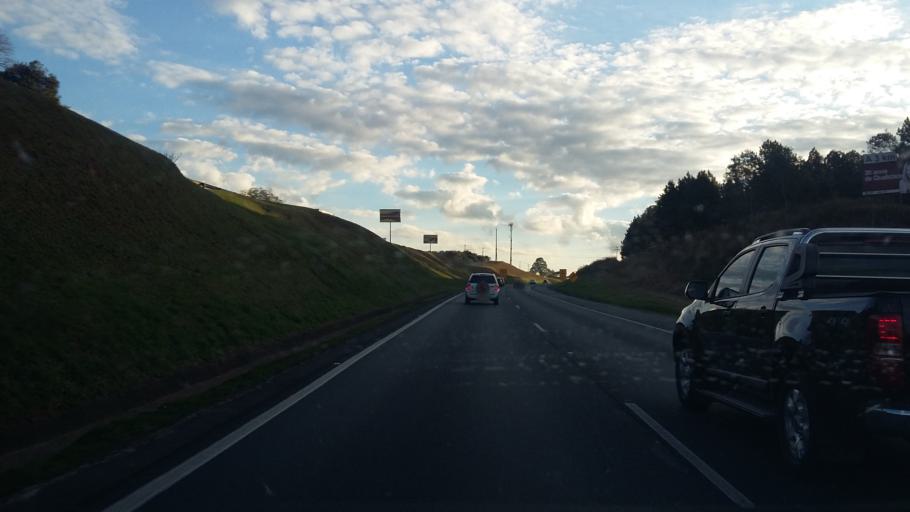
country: BR
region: Parana
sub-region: Campo Largo
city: Campo Largo
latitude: -25.4463
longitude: -49.4718
